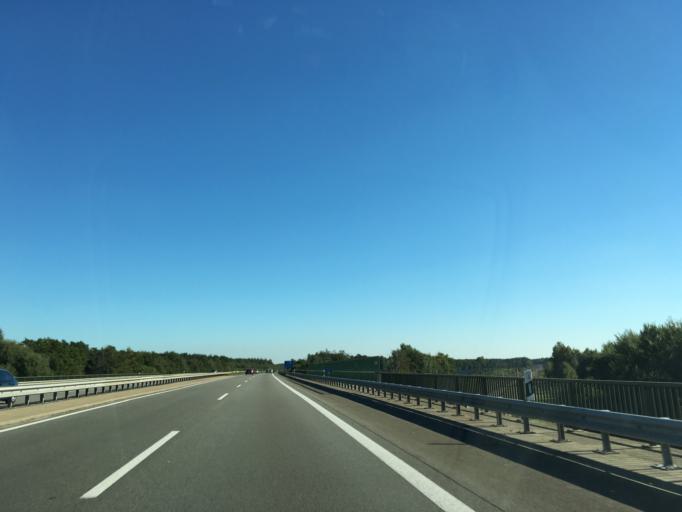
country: DE
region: Lower Saxony
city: Winsen
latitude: 53.3354
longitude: 10.2463
